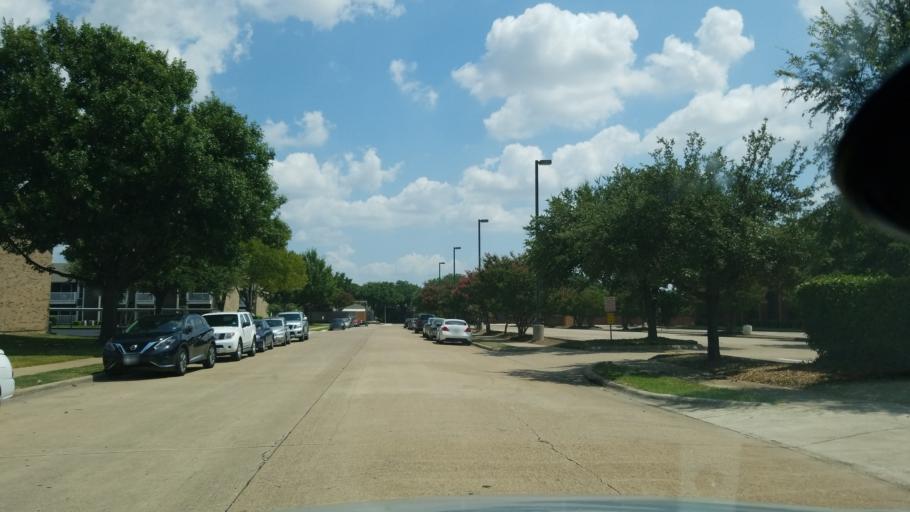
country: US
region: Texas
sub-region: Dallas County
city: Richardson
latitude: 32.9272
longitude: -96.7344
